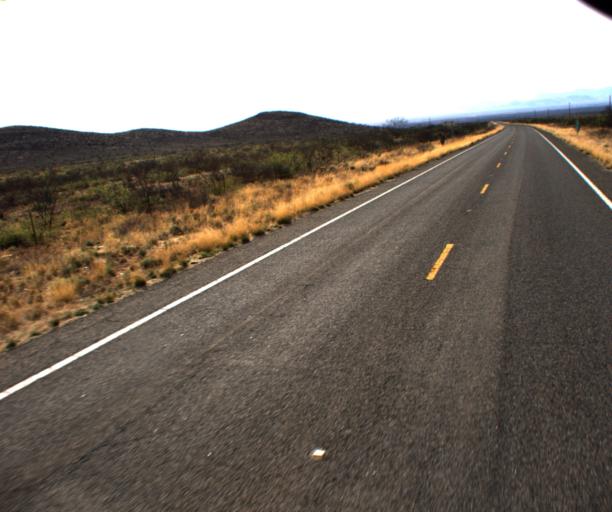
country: US
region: Arizona
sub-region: Cochise County
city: Willcox
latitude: 32.1858
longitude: -109.6756
